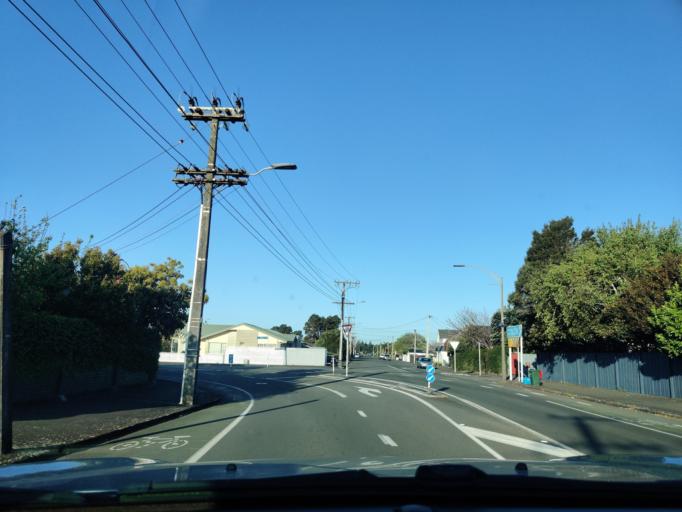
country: NZ
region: Taranaki
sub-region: New Plymouth District
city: New Plymouth
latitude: -39.0671
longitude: 174.0655
